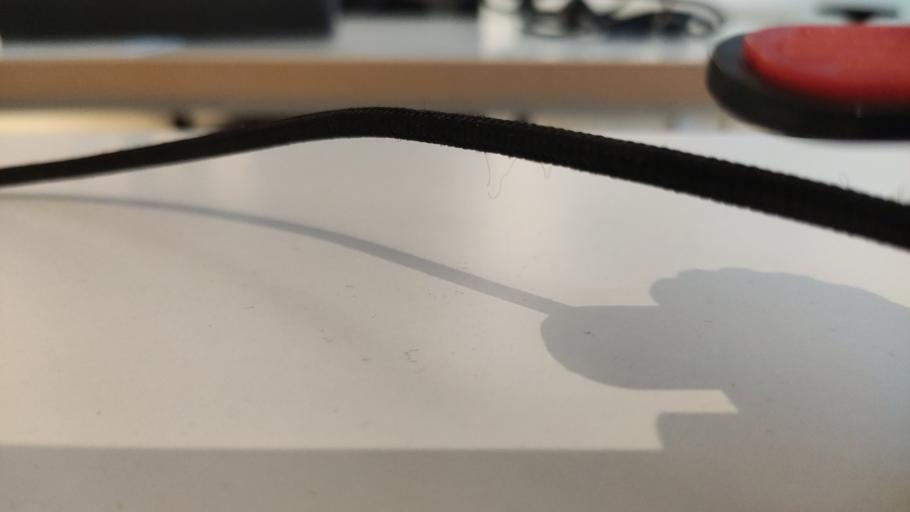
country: RU
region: Moskovskaya
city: Novopetrovskoye
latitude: 55.8626
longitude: 36.3869
